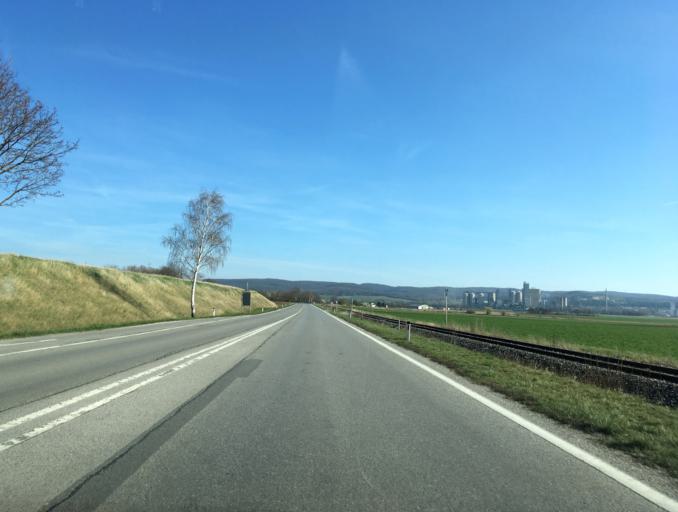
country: AT
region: Lower Austria
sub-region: Politischer Bezirk Bruck an der Leitha
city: Gotzendorf an der Leitha
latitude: 48.0044
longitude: 16.5908
